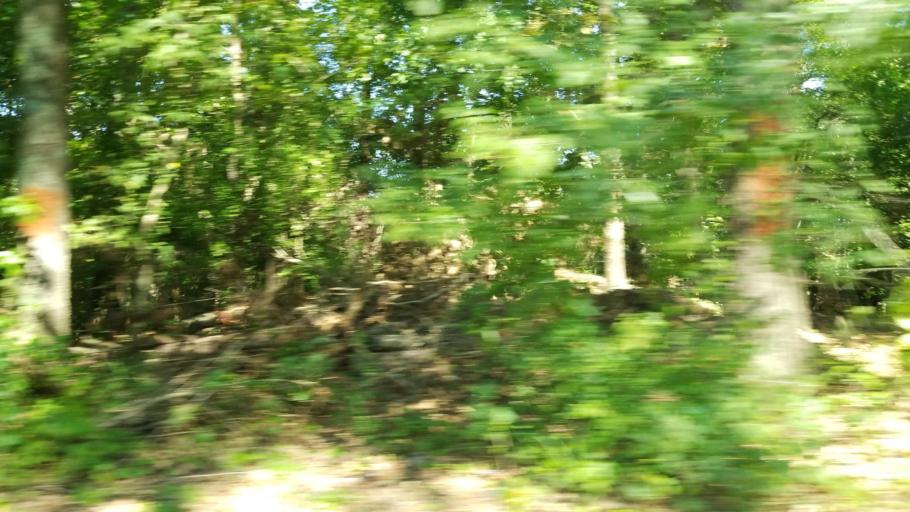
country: US
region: Illinois
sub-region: Saline County
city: Carrier Mills
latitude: 37.7957
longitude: -88.6471
